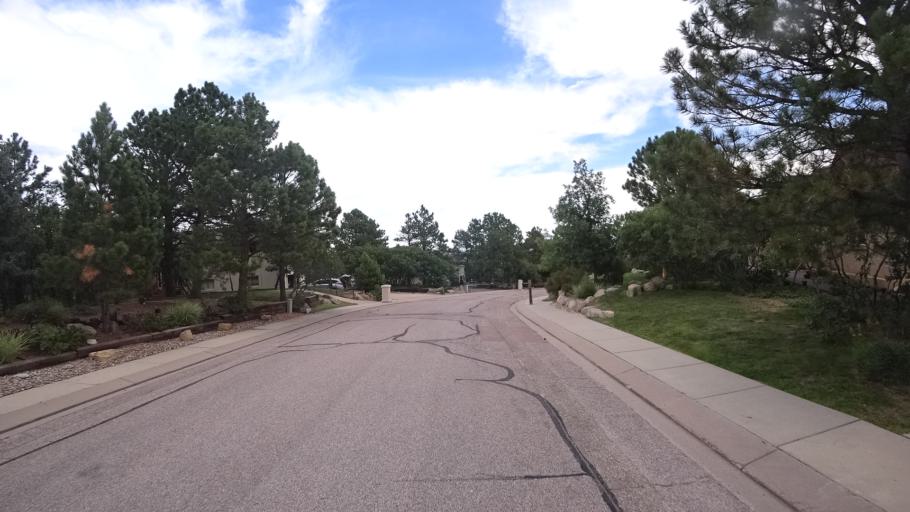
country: US
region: Colorado
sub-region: El Paso County
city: Colorado Springs
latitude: 38.9048
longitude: -104.8477
